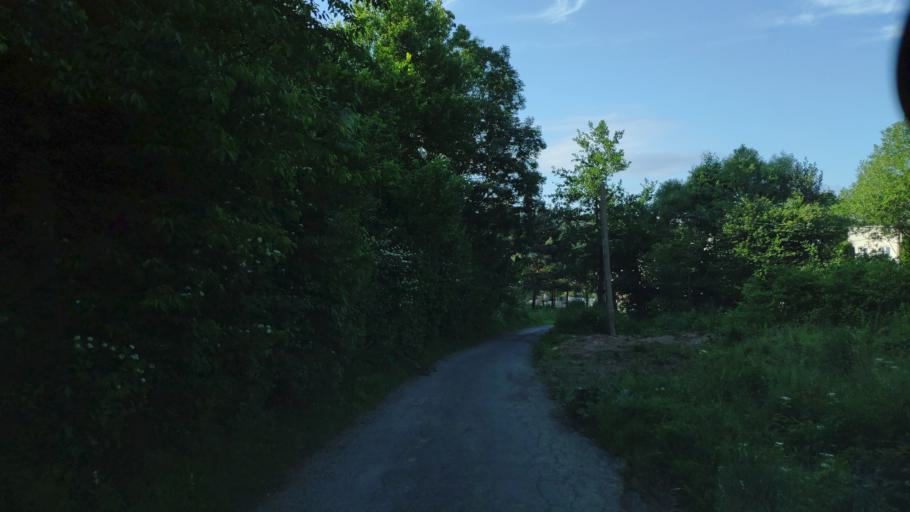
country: SK
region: Presovsky
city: Vranov nad Topl'ou
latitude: 48.8264
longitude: 21.5771
